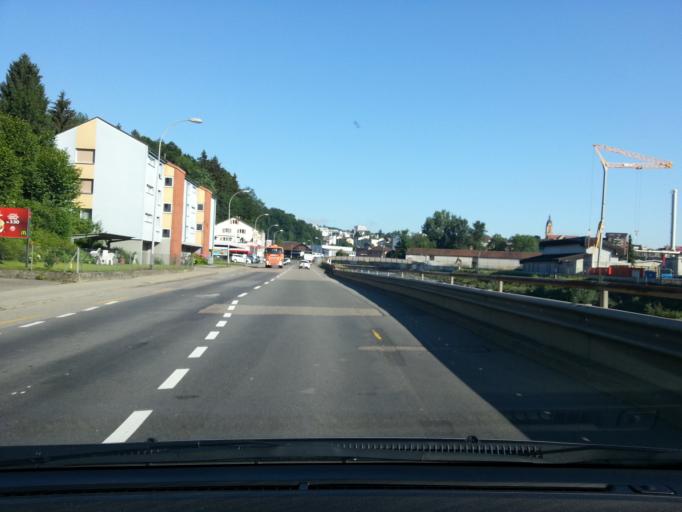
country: CH
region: Lucerne
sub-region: Hochdorf District
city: Emmen
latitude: 47.0697
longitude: 8.2778
